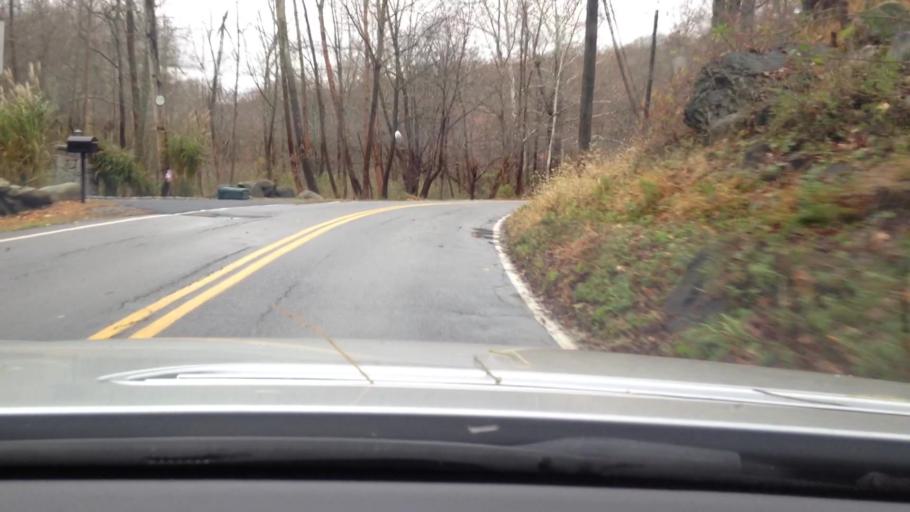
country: US
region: New York
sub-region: Westchester County
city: Croton-on-Hudson
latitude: 41.2342
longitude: -73.8886
